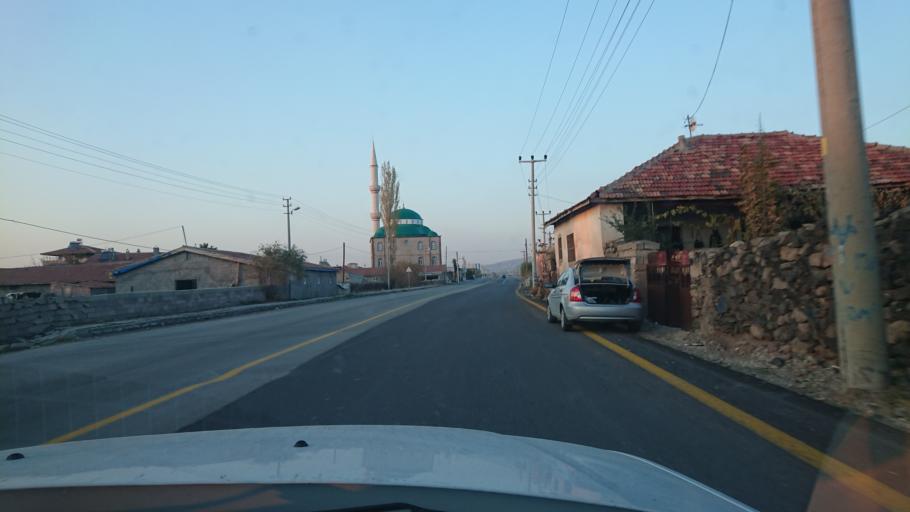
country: TR
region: Aksaray
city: Aksaray
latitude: 38.3178
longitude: 34.0532
